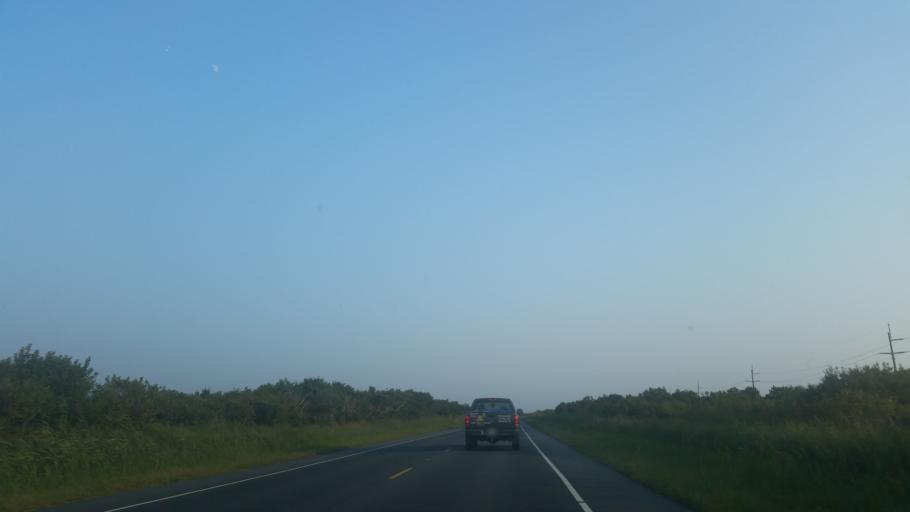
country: US
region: North Carolina
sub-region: Dare County
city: Wanchese
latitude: 35.6445
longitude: -75.4749
